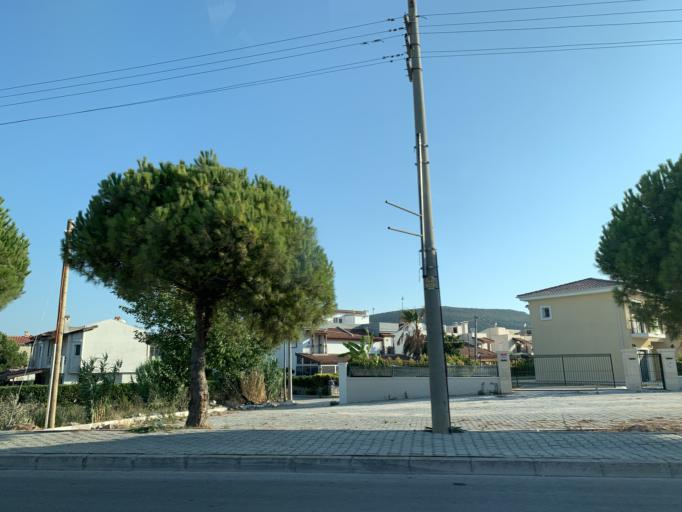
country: TR
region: Izmir
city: Alacati
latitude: 38.3054
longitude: 26.3585
